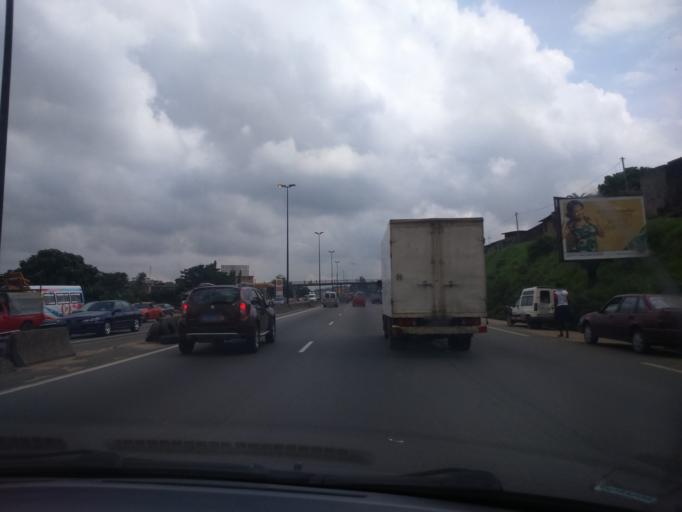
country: CI
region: Lagunes
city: Abidjan
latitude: 5.3624
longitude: -4.0236
